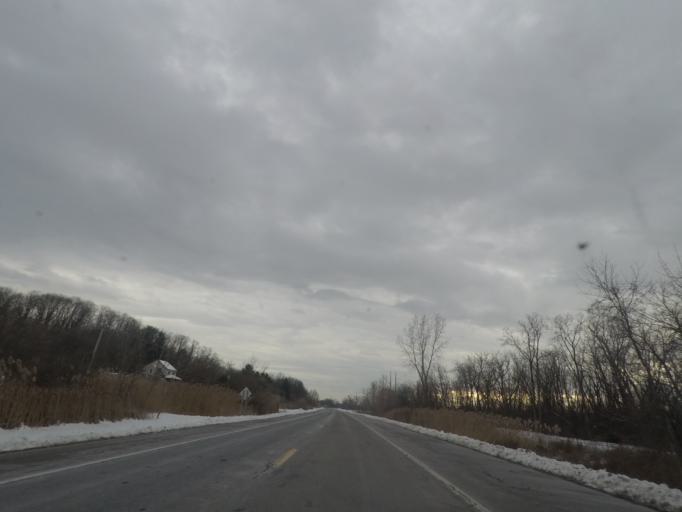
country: US
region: New York
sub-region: Rensselaer County
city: Hampton Manor
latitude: 42.6162
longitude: -73.7468
